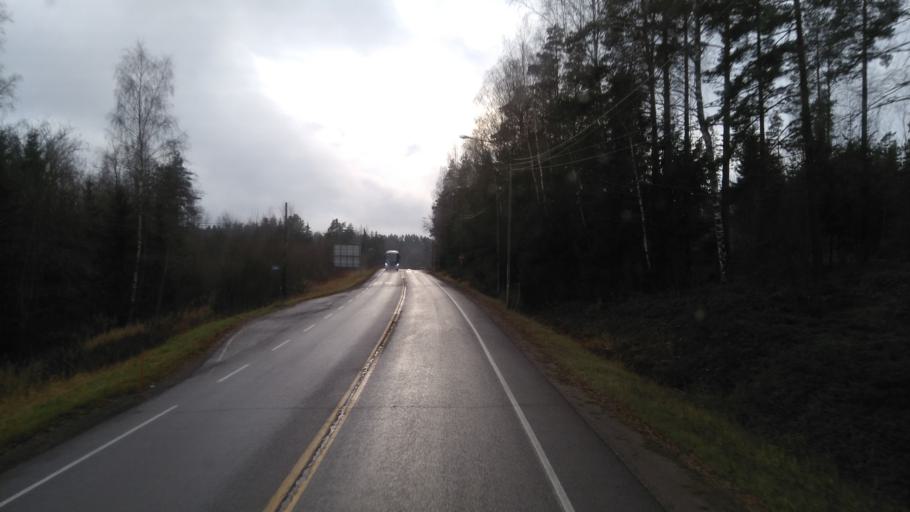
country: FI
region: Uusimaa
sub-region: Porvoo
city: Porvoo
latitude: 60.4169
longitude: 25.7043
